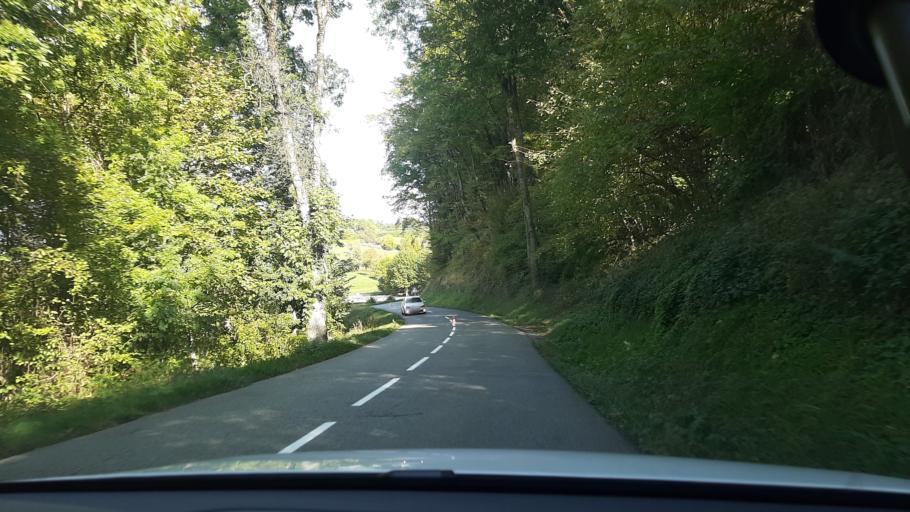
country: FR
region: Rhone-Alpes
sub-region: Departement de l'Isere
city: Pontcharra
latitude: 45.4498
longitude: 6.0530
